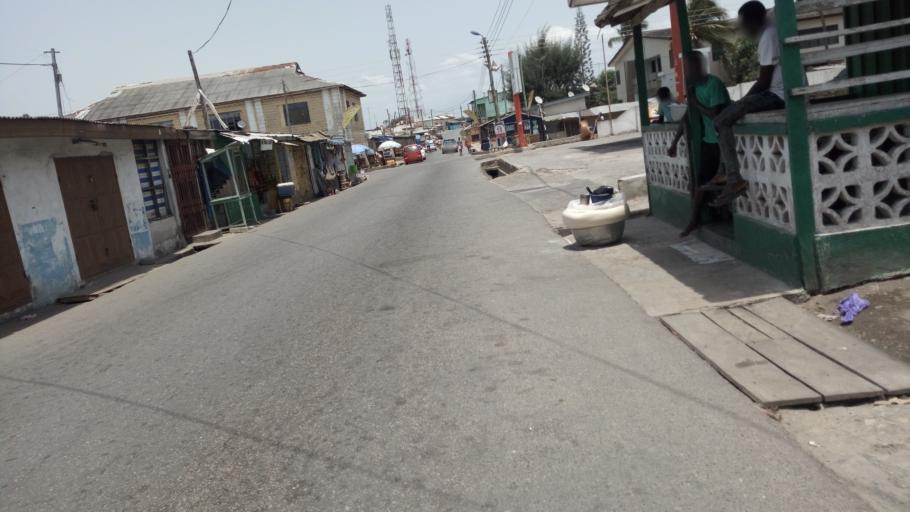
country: GH
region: Central
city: Winneba
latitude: 5.3473
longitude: -0.6258
